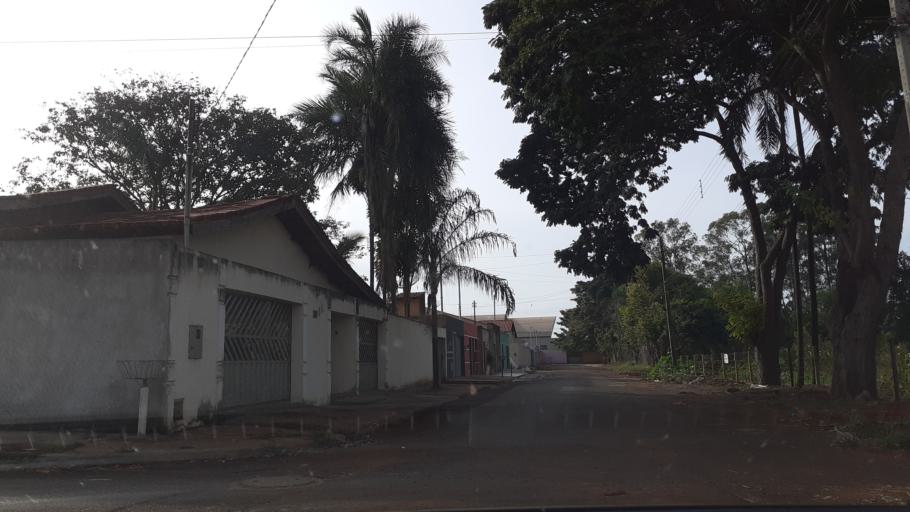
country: BR
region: Goias
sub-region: Itumbiara
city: Itumbiara
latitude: -18.4240
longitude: -49.2496
